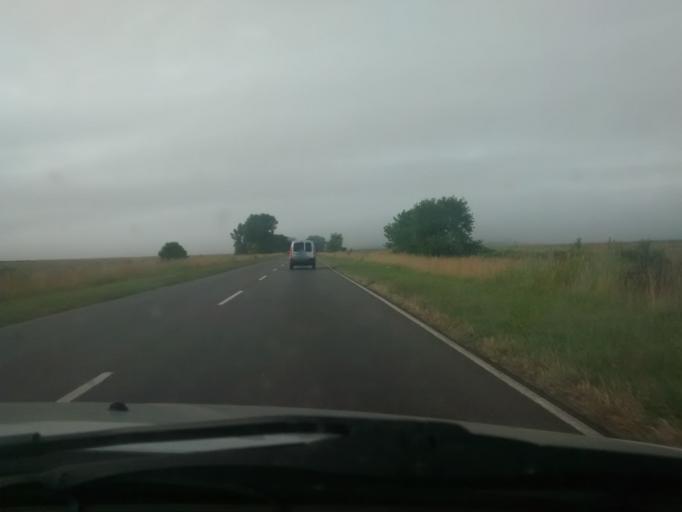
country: AR
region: Buenos Aires
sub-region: Partido de Brandsen
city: Brandsen
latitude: -35.3469
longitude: -58.2469
